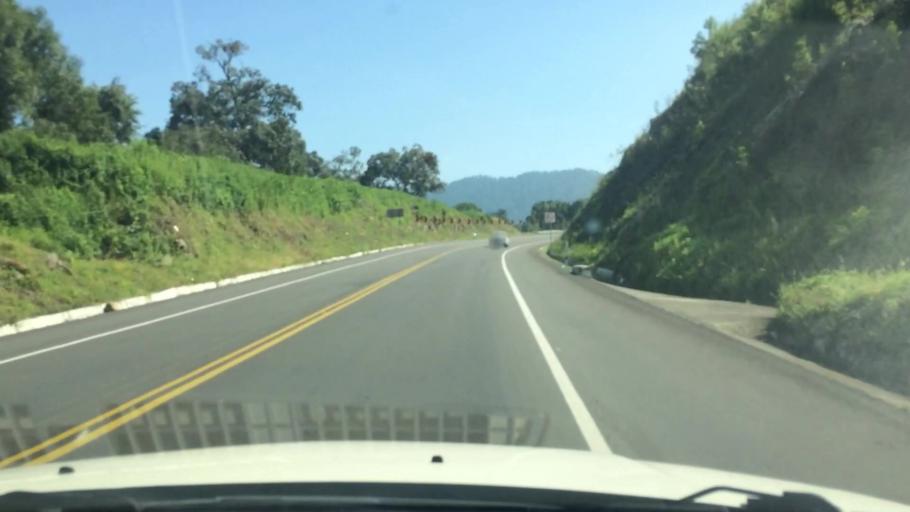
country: MX
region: Mexico
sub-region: Valle de Bravo
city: Santa Maria Pipioltepec (Pipioltepec)
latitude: 19.2182
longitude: -100.0980
